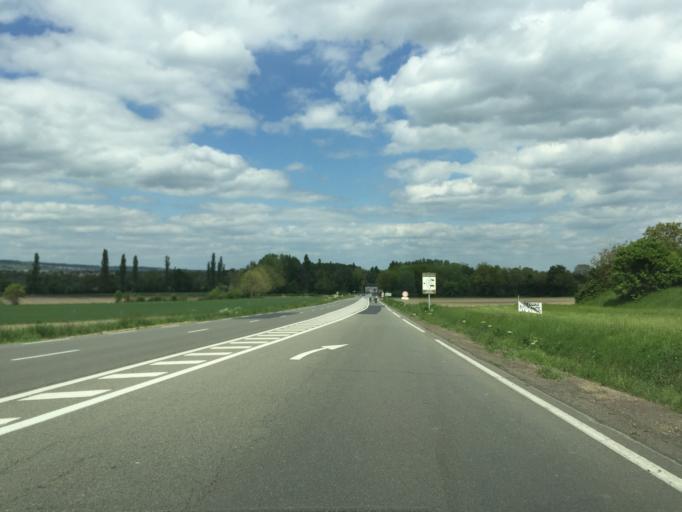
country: FR
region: Auvergne
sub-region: Departement du Puy-de-Dome
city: Saint-Bonnet-pres-Riom
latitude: 45.9430
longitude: 3.1554
